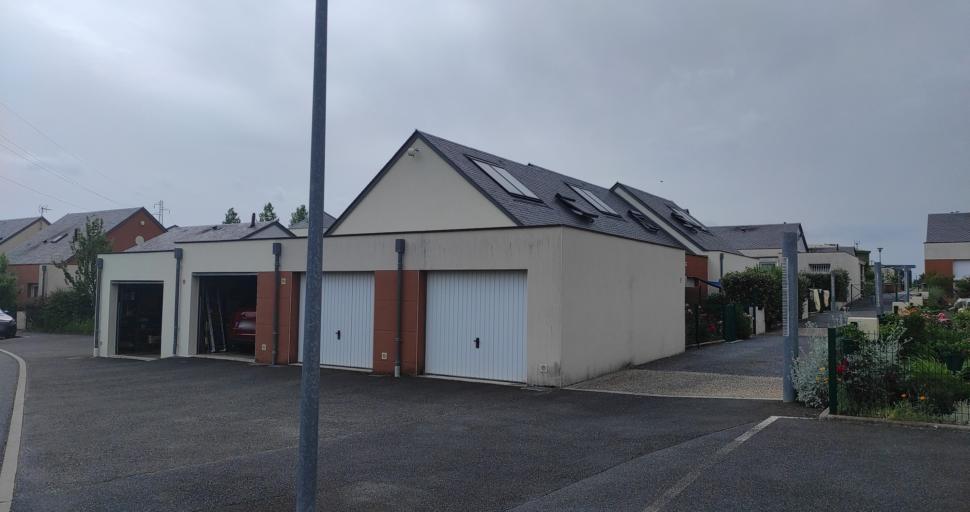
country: FR
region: Midi-Pyrenees
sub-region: Departement de l'Aveyron
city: Olemps
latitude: 44.3415
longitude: 2.5513
